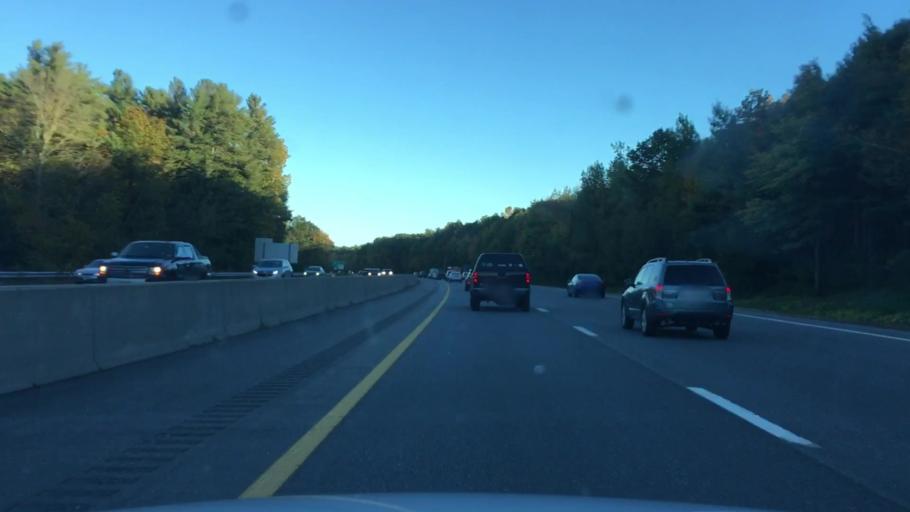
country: US
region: New Hampshire
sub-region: Rockingham County
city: Hampton Falls
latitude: 42.9681
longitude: -70.8880
